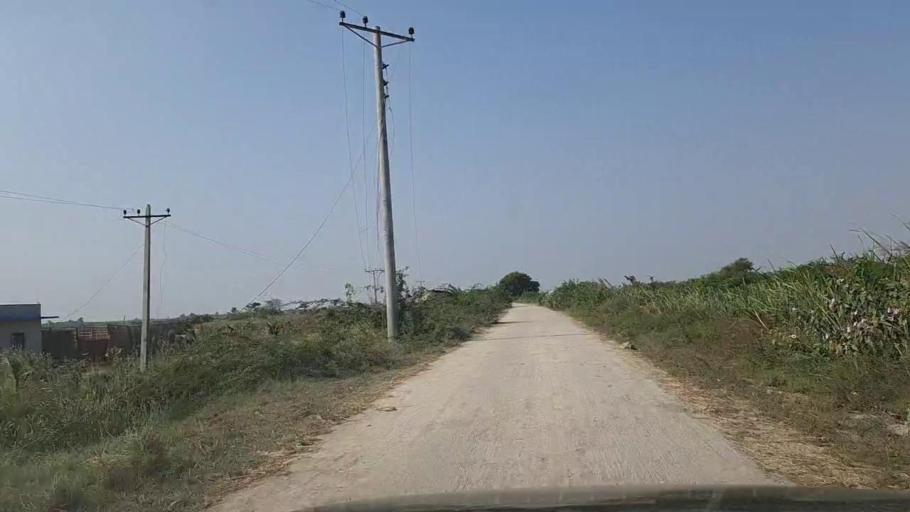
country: PK
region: Sindh
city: Thatta
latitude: 24.7380
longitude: 67.7552
